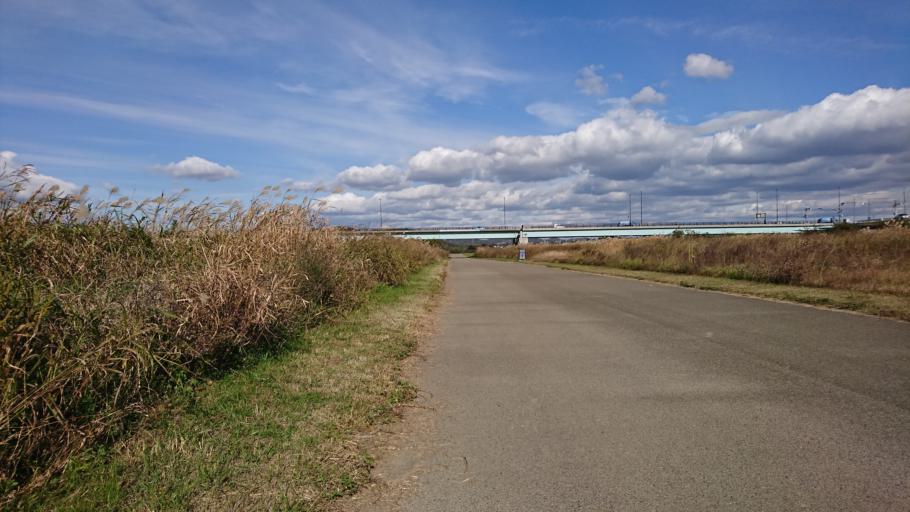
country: JP
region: Hyogo
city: Kakogawacho-honmachi
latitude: 34.7875
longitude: 134.8659
